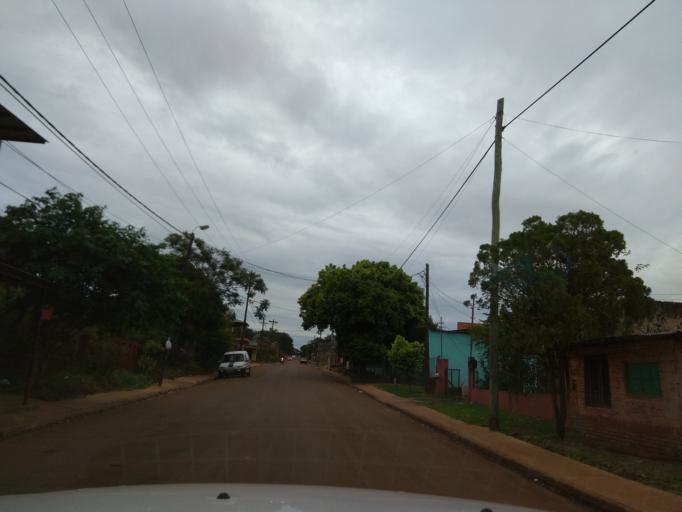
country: AR
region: Misiones
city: Garupa
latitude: -27.4422
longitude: -55.8658
